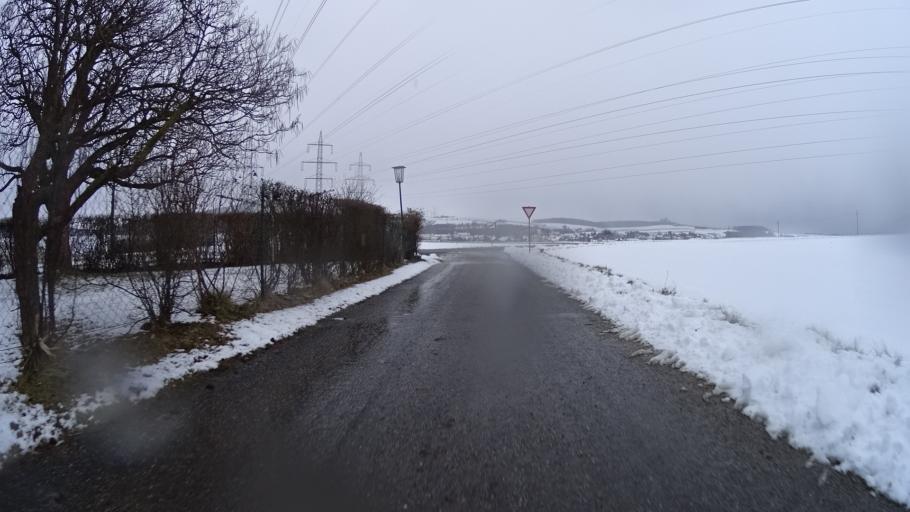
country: AT
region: Lower Austria
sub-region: Politischer Bezirk Korneuburg
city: Niederhollabrunn
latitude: 48.4021
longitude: 16.2839
